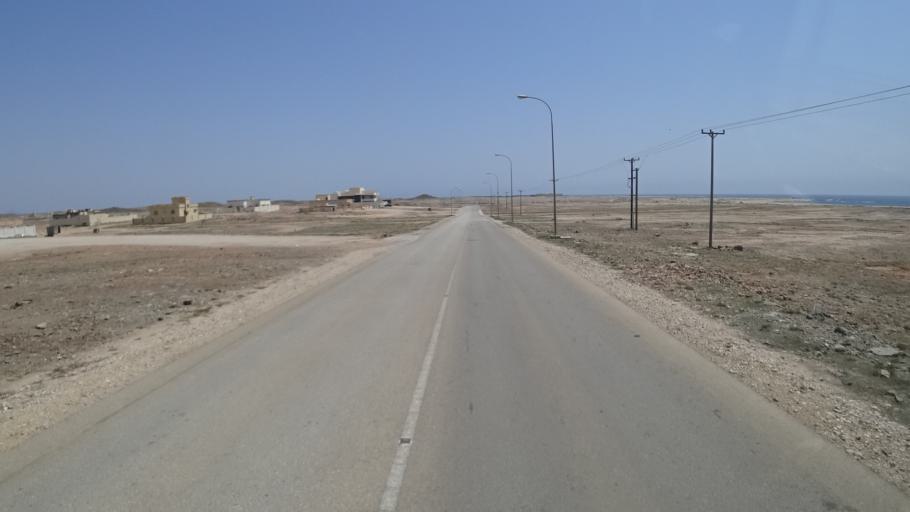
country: OM
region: Zufar
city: Salalah
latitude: 16.9749
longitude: 54.7154
